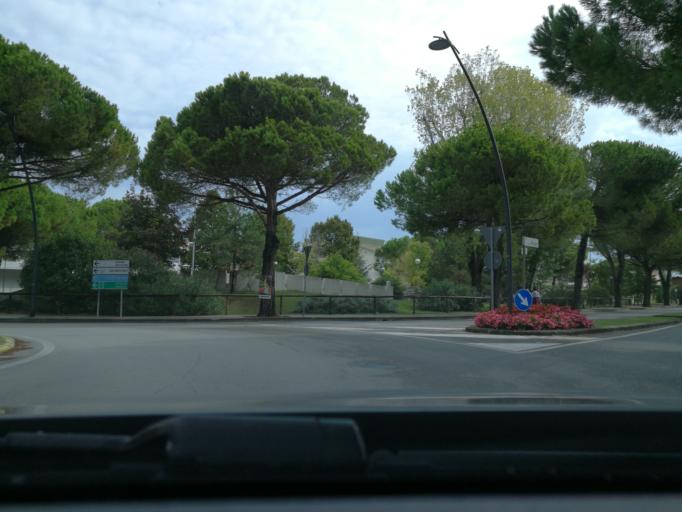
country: IT
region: Veneto
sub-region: Provincia di Venezia
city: Bibione
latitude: 45.6426
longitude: 13.0549
